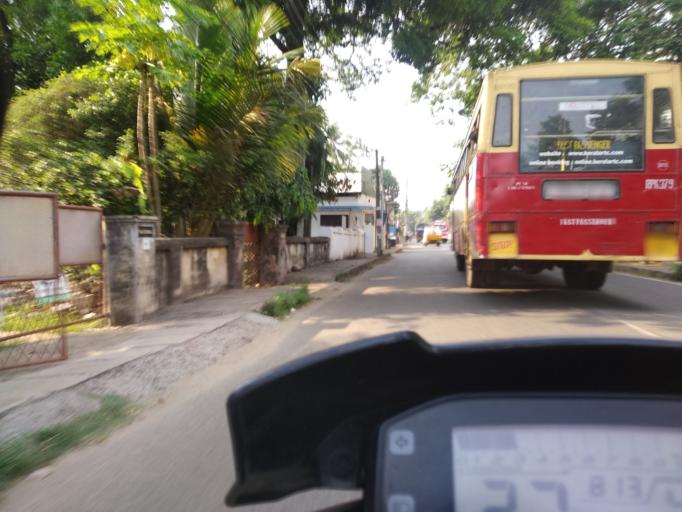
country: IN
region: Kerala
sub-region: Alappuzha
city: Arukutti
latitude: 9.9523
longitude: 76.3457
